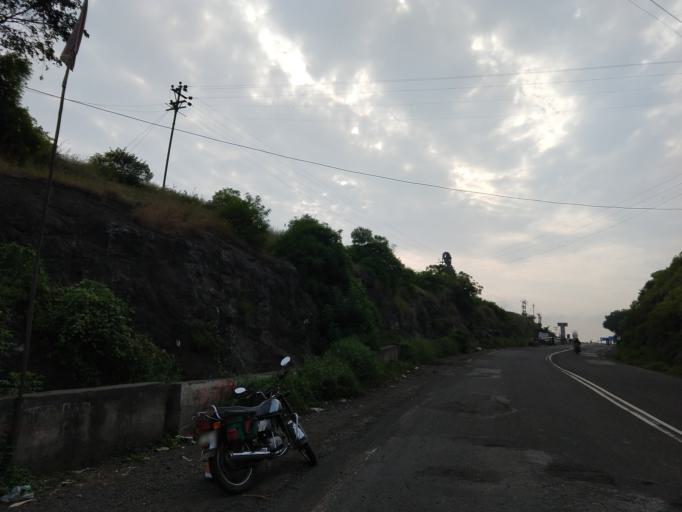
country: IN
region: Maharashtra
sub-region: Pune Division
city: Sasvad
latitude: 18.4159
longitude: 74.0047
